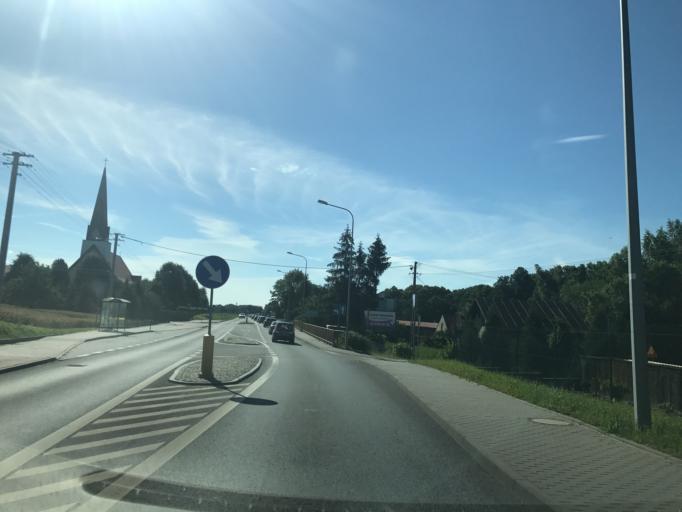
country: PL
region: Kujawsko-Pomorskie
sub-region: Powiat tucholski
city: Kesowo
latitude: 53.6466
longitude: 17.7087
